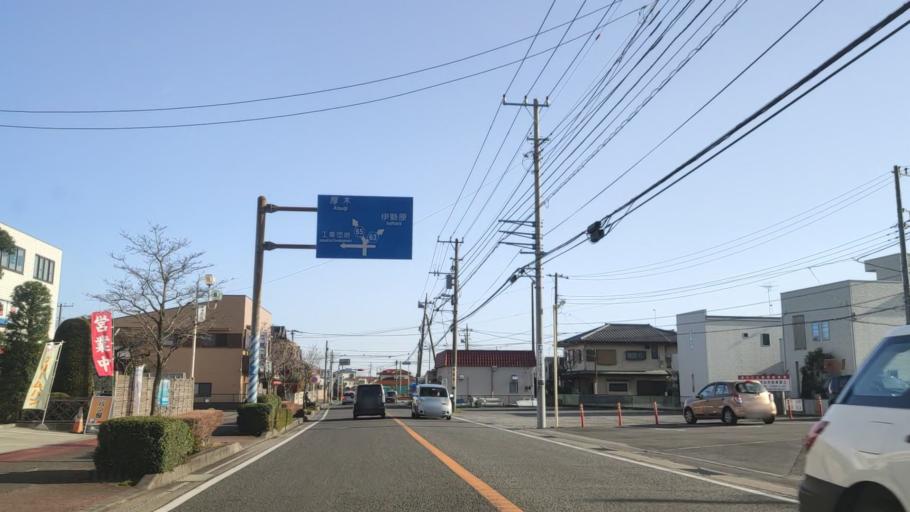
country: JP
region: Kanagawa
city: Zama
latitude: 35.5072
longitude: 139.3399
